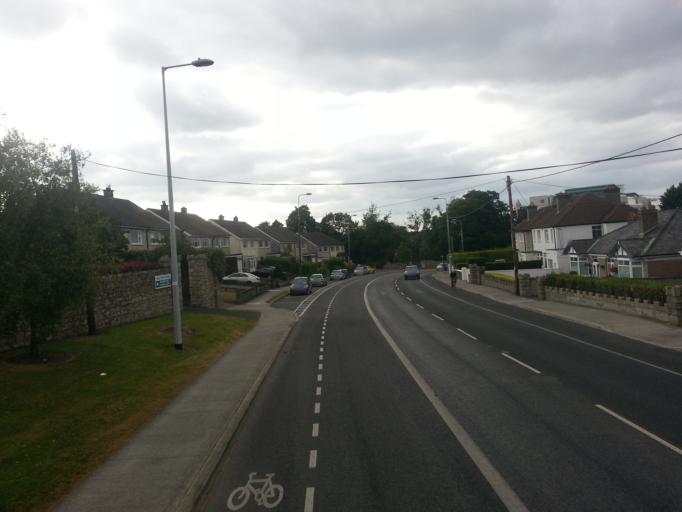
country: IE
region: Leinster
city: Balally
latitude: 53.2837
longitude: -6.2352
